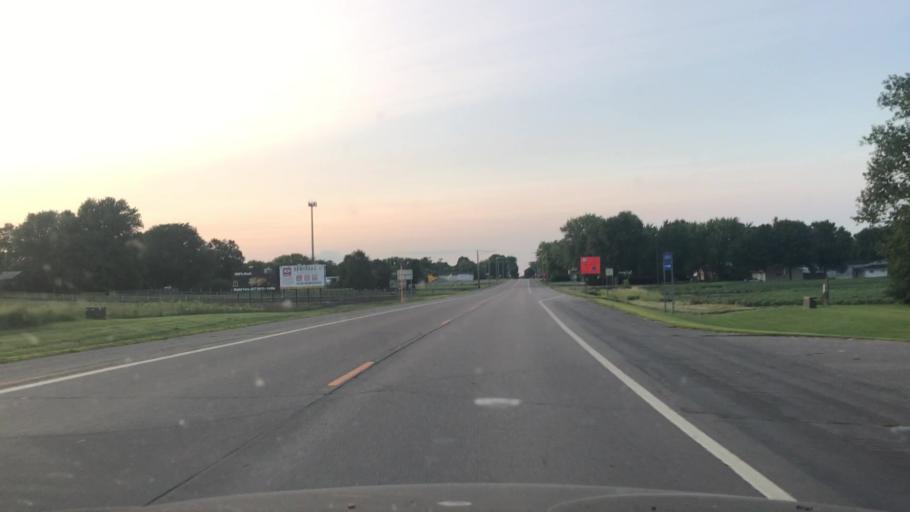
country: US
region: Minnesota
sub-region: Redwood County
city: Redwood Falls
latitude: 44.5271
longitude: -95.1195
